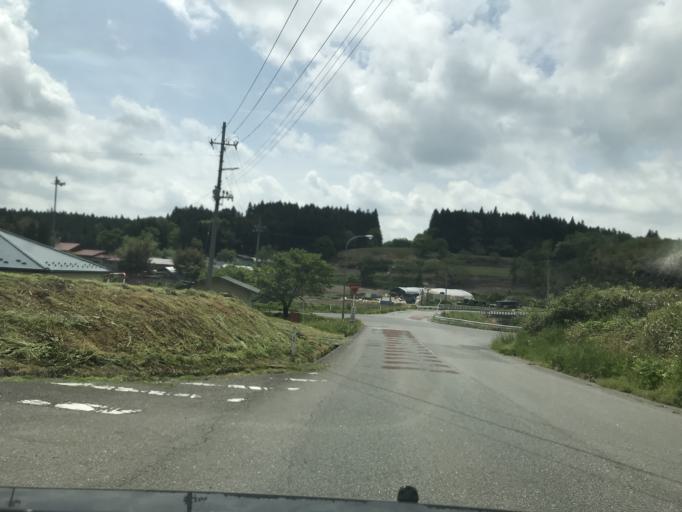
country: JP
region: Miyagi
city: Furukawa
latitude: 38.7322
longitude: 140.9276
